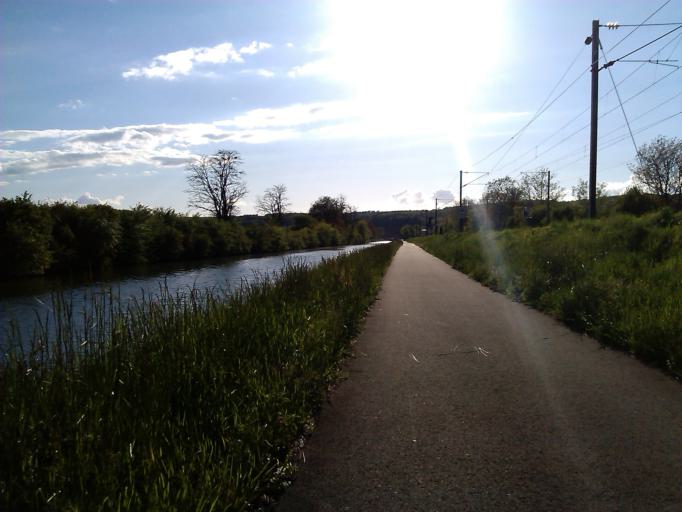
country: FR
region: Franche-Comte
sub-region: Departement du Doubs
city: Clerval
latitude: 47.4161
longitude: 6.5320
